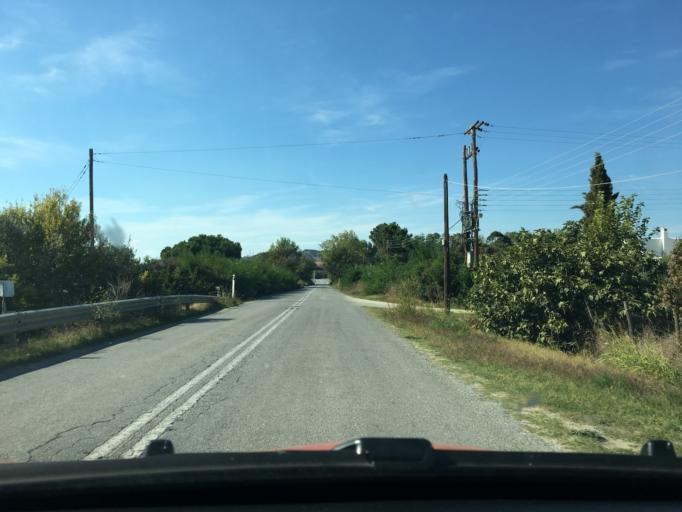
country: GR
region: Central Macedonia
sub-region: Nomos Chalkidikis
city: Nea Roda
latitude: 40.3634
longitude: 23.9247
